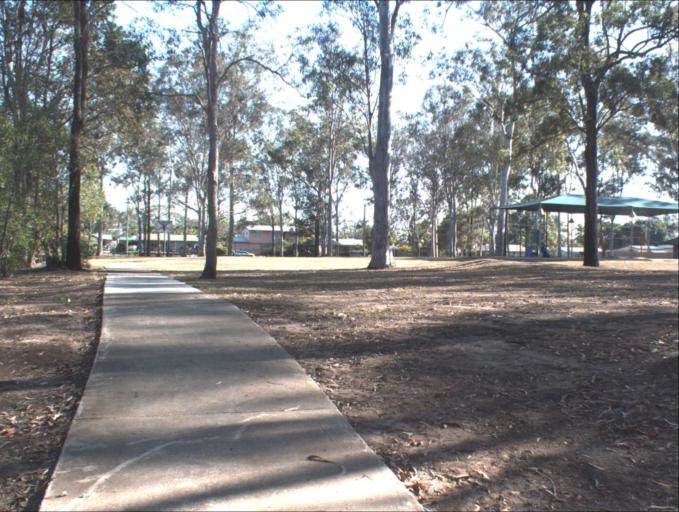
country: AU
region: Queensland
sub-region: Gold Coast
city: Yatala
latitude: -27.7052
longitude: 153.2222
